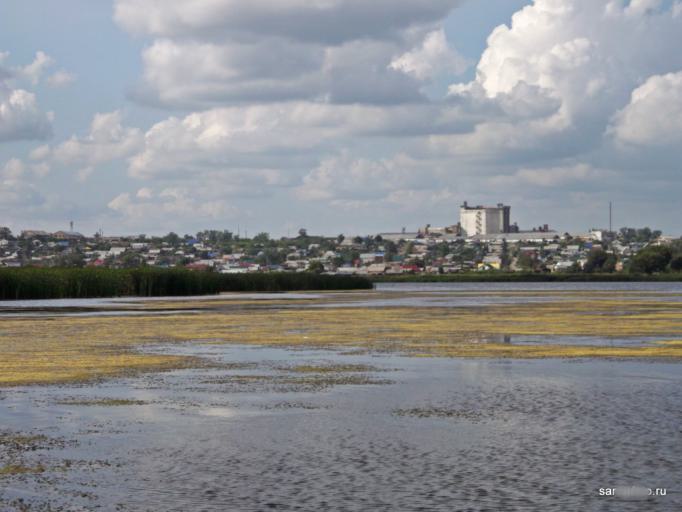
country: RU
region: Chelyabinsk
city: Troitsk
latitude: 54.0849
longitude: 61.5860
